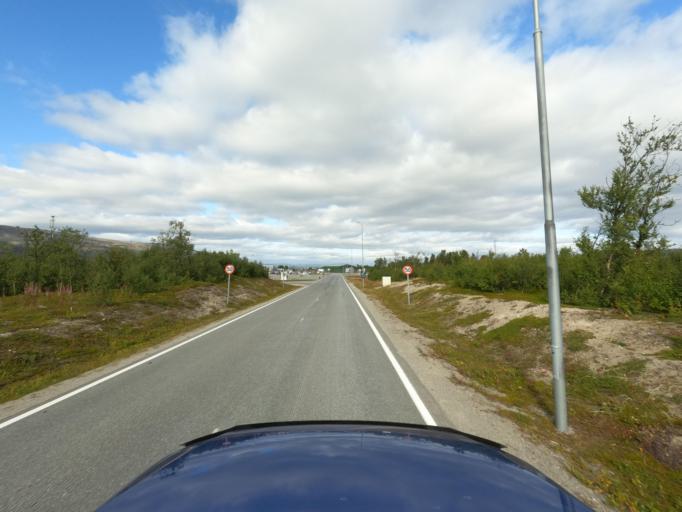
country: NO
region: Finnmark Fylke
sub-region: Porsanger
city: Lakselv
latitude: 70.0648
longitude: 24.9849
